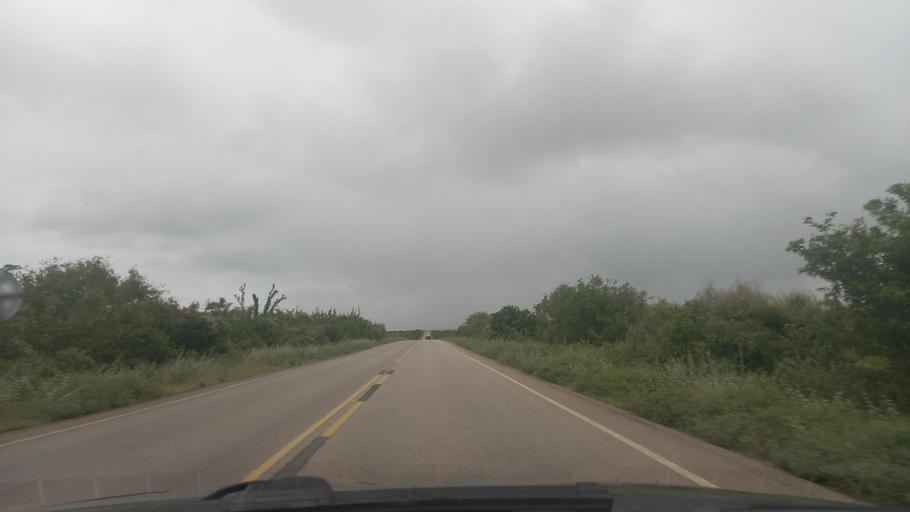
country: BR
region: Bahia
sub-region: Paulo Afonso
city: Paulo Afonso
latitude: -9.3318
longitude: -38.2860
